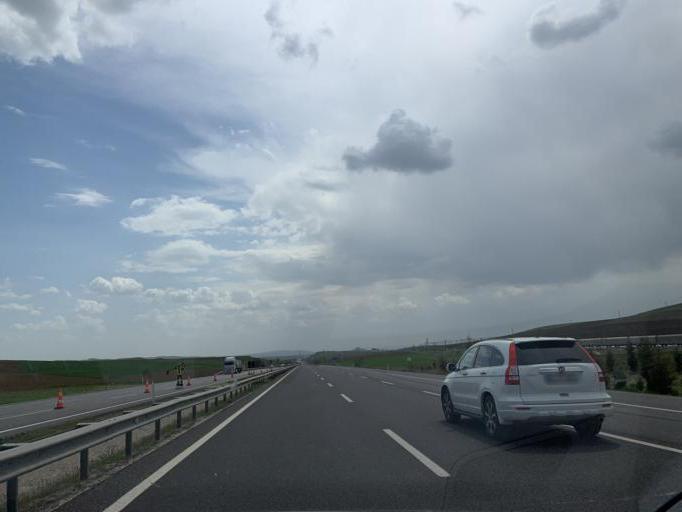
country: TR
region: Ankara
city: Polatli
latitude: 39.6138
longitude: 32.1857
